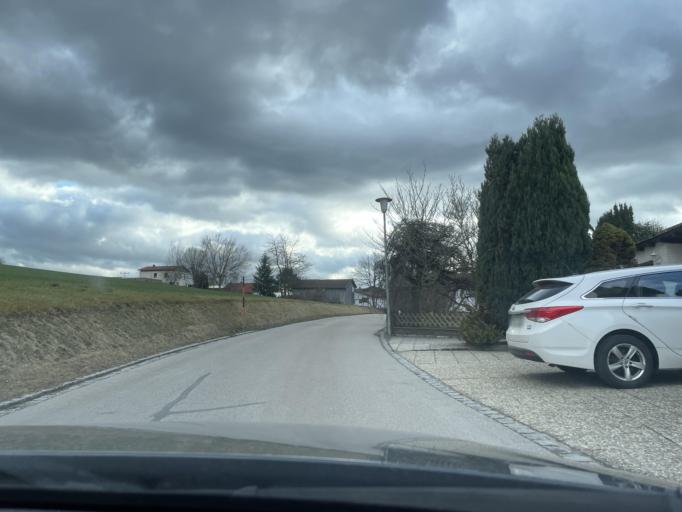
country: DE
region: Bavaria
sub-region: Upper Palatinate
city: Runding
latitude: 49.2151
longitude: 12.7714
